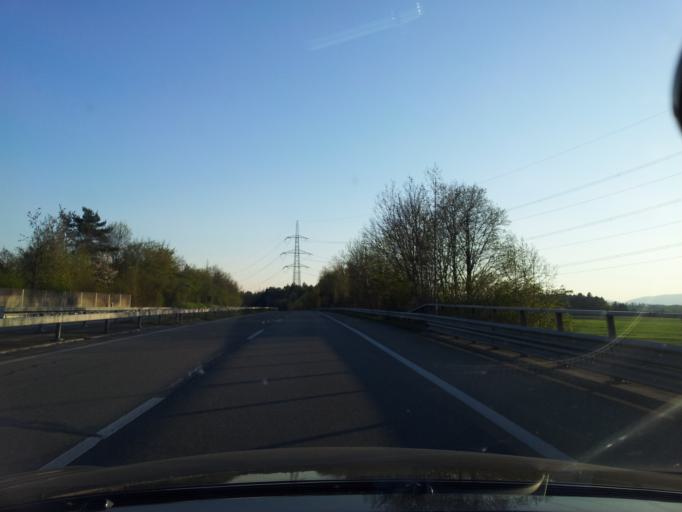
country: CH
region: Bern
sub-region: Seeland District
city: Lyss
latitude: 47.0828
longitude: 7.2959
